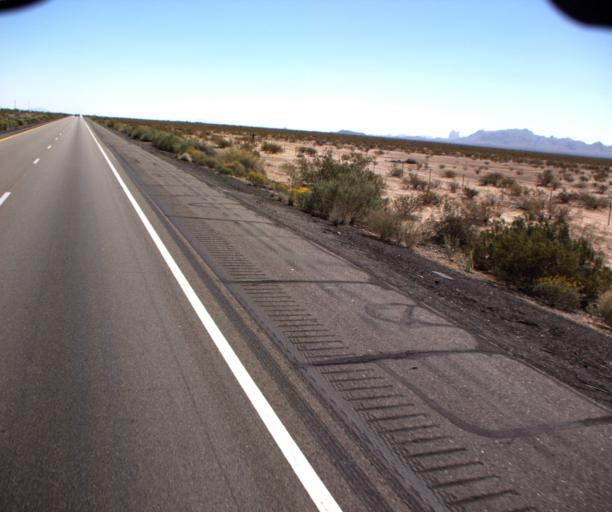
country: US
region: Arizona
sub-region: La Paz County
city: Salome
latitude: 33.5941
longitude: -113.5214
